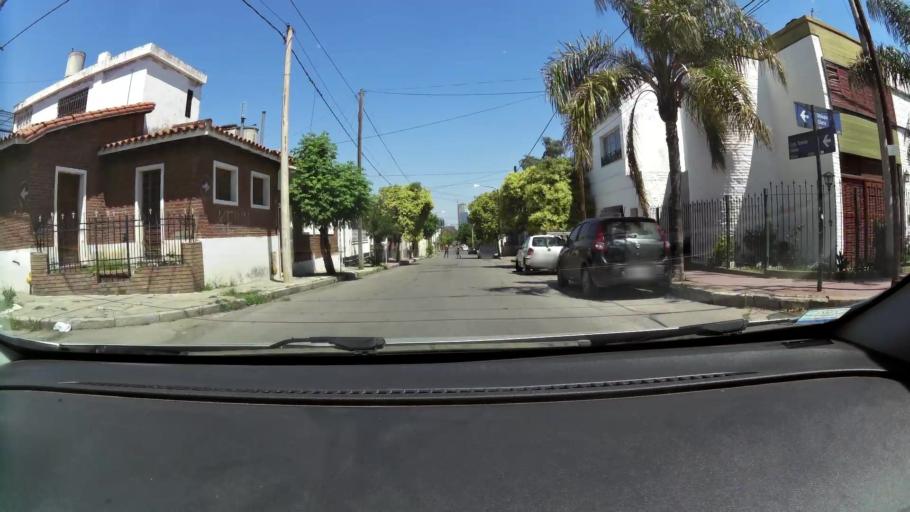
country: AR
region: Cordoba
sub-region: Departamento de Capital
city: Cordoba
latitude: -31.3942
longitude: -64.1982
